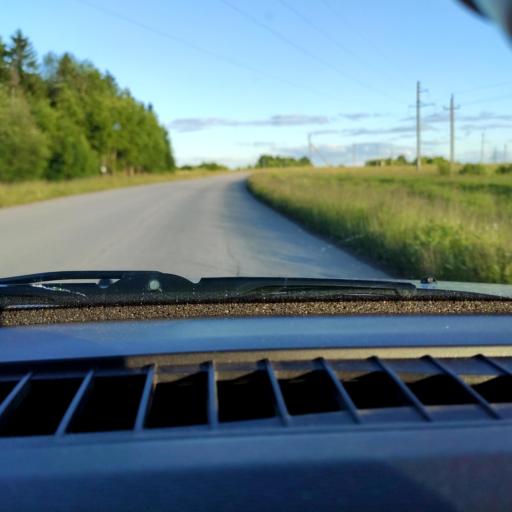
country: RU
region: Perm
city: Novyye Lyady
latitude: 58.1920
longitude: 56.5390
